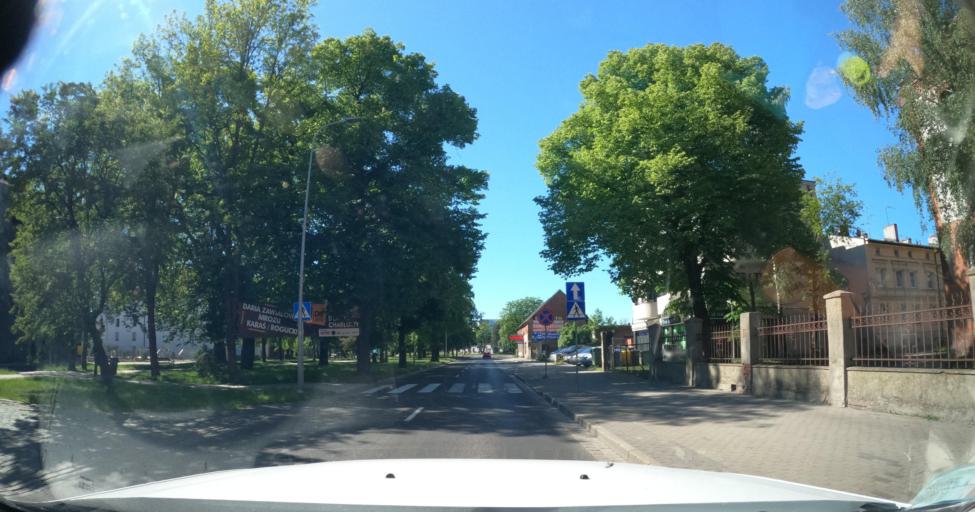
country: PL
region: Pomeranian Voivodeship
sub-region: Slupsk
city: Slupsk
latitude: 54.4719
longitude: 17.0278
